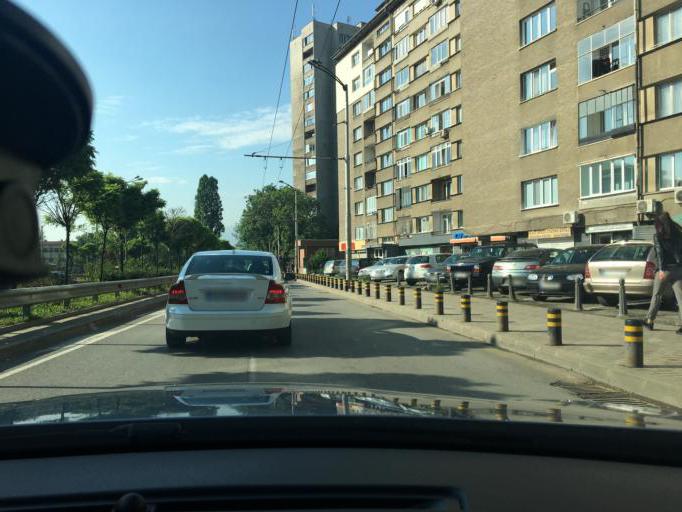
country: BG
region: Sofia-Capital
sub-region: Stolichna Obshtina
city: Sofia
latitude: 42.6833
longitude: 23.3012
